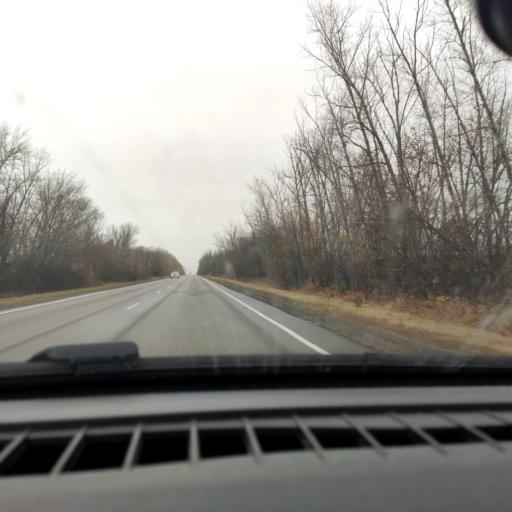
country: RU
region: Voronezj
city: Ostrogozhsk
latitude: 51.0083
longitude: 38.9972
